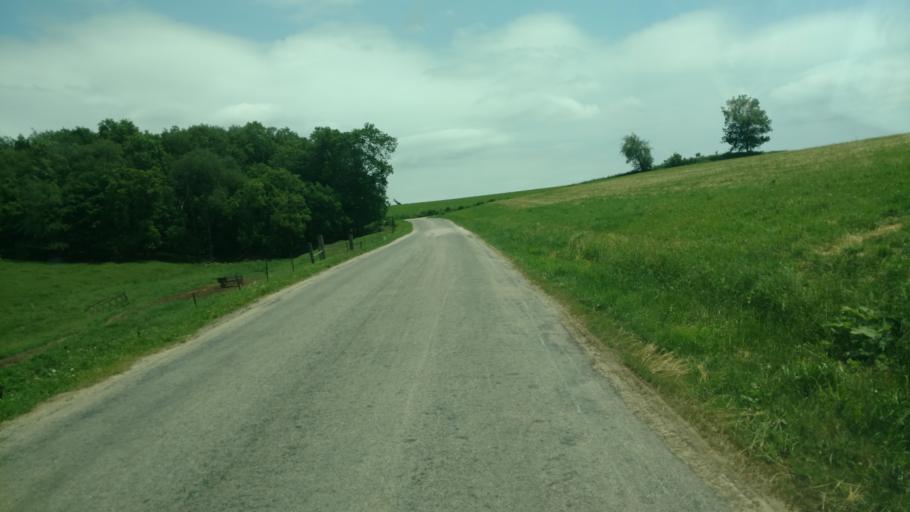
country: US
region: Wisconsin
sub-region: Monroe County
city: Cashton
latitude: 43.6875
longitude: -90.6771
